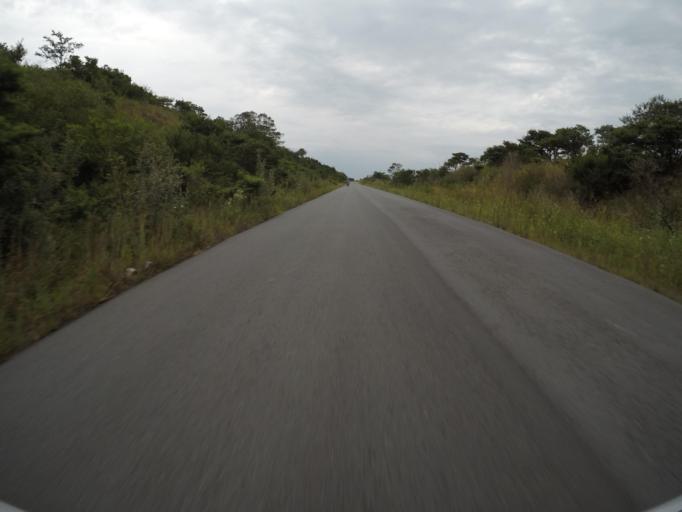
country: ZA
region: Eastern Cape
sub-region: Buffalo City Metropolitan Municipality
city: East London
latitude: -32.9612
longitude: 27.9005
